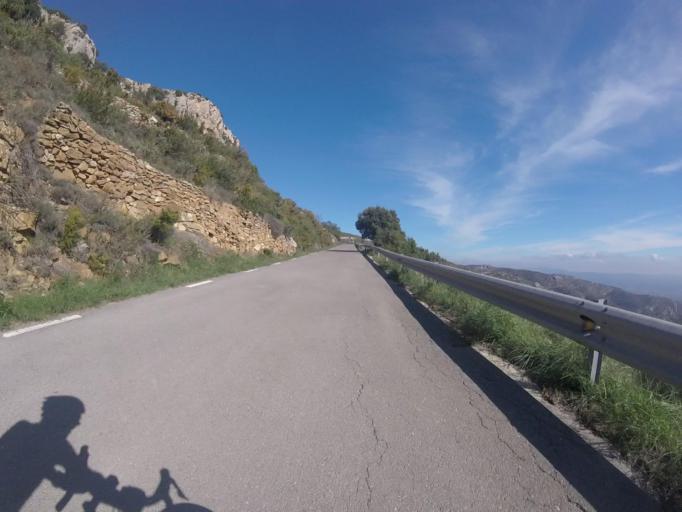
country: ES
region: Valencia
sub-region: Provincia de Castello
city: Sarratella
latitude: 40.2899
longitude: 0.0311
